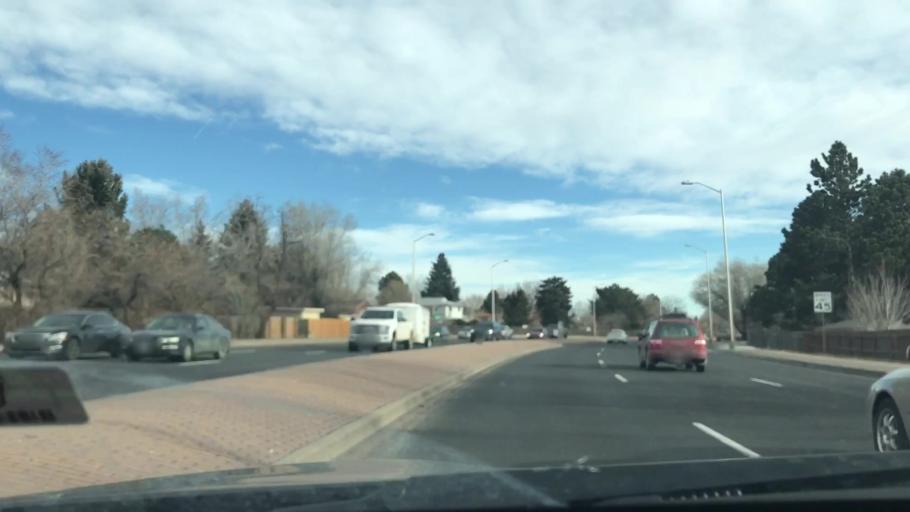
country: US
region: Colorado
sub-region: El Paso County
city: Cimarron Hills
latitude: 38.9003
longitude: -104.7652
